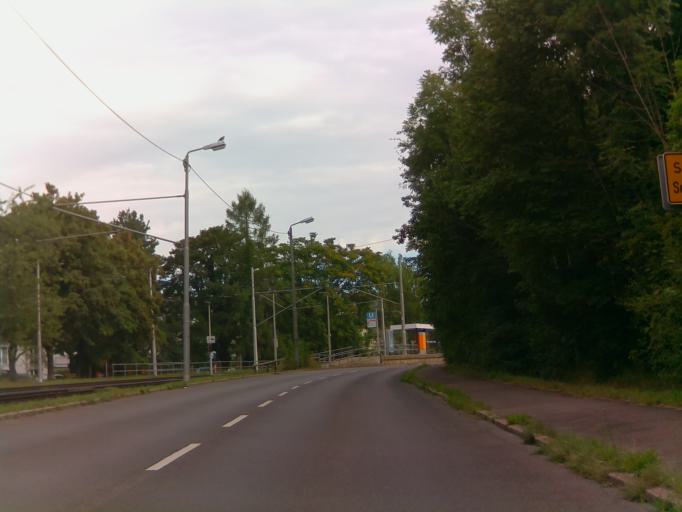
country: DE
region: Baden-Wuerttemberg
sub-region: Regierungsbezirk Stuttgart
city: Leinfelden-Echterdingen
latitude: 48.7395
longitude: 9.1524
